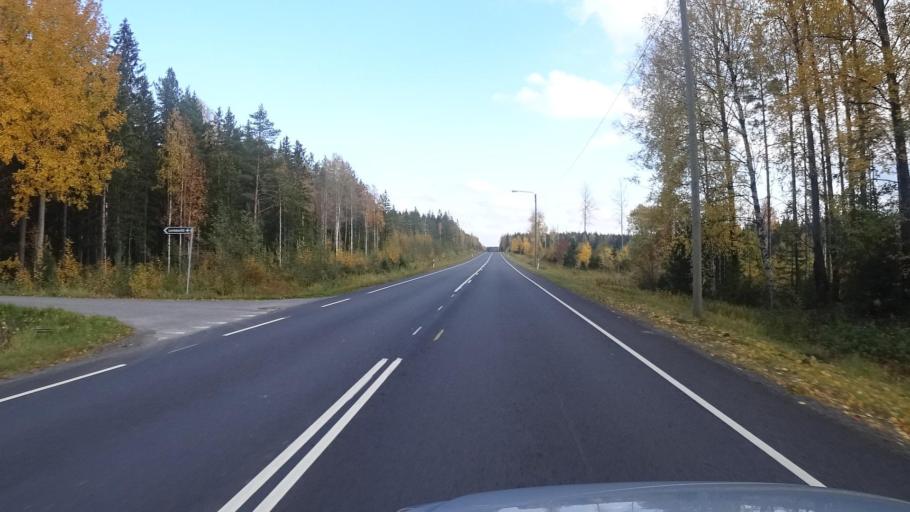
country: FI
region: Satakunta
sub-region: Rauma
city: Eura
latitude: 61.1162
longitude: 22.1928
